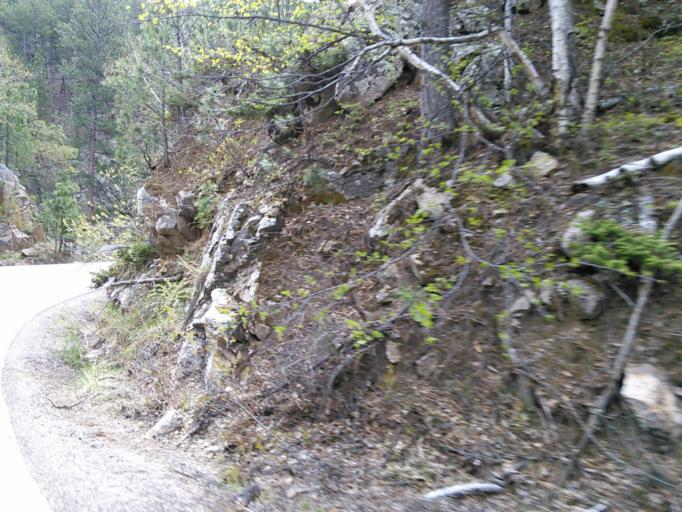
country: US
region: South Dakota
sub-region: Custer County
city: Custer
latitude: 43.8007
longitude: -103.4364
